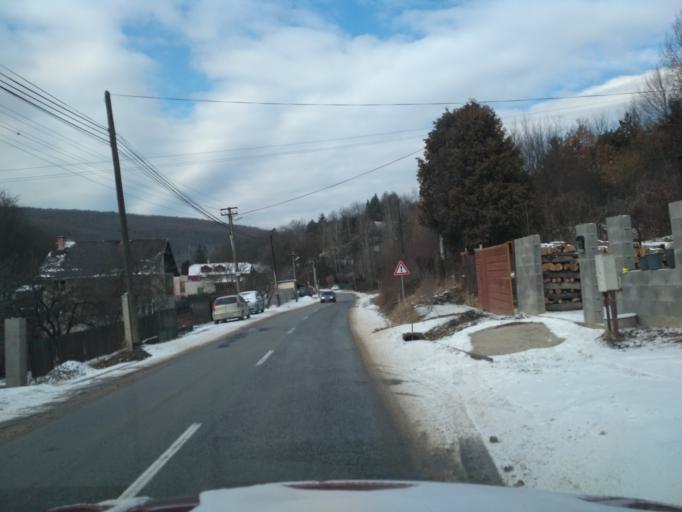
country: SK
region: Kosicky
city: Kosice
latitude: 48.7251
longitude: 21.1511
